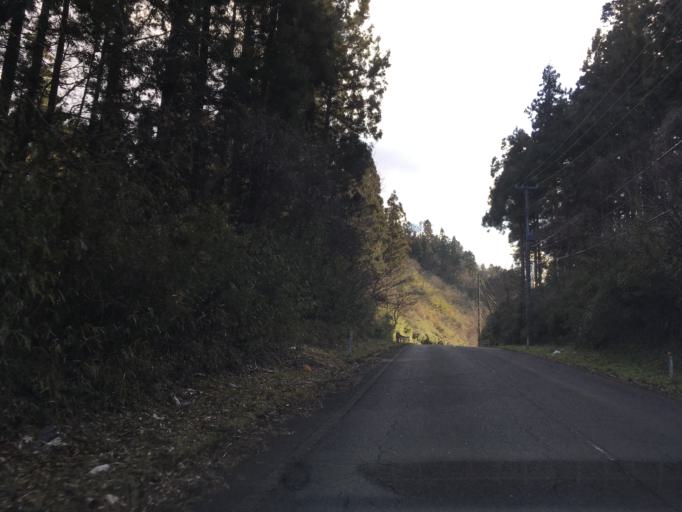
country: JP
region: Iwate
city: Ichinoseki
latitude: 38.8125
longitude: 140.9971
